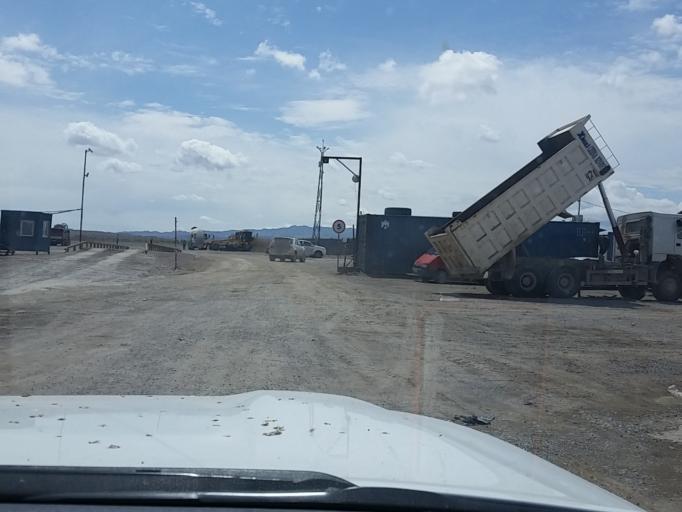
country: KZ
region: Almaty Oblysy
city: Kegen
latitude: 43.7527
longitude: 79.1102
